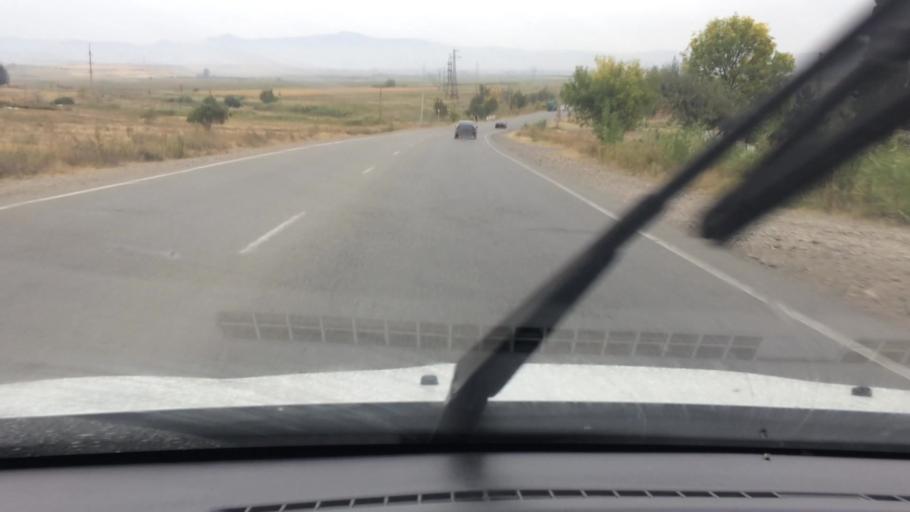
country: GE
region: Kvemo Kartli
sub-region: Marneuli
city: Marneuli
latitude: 41.5249
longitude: 44.7775
